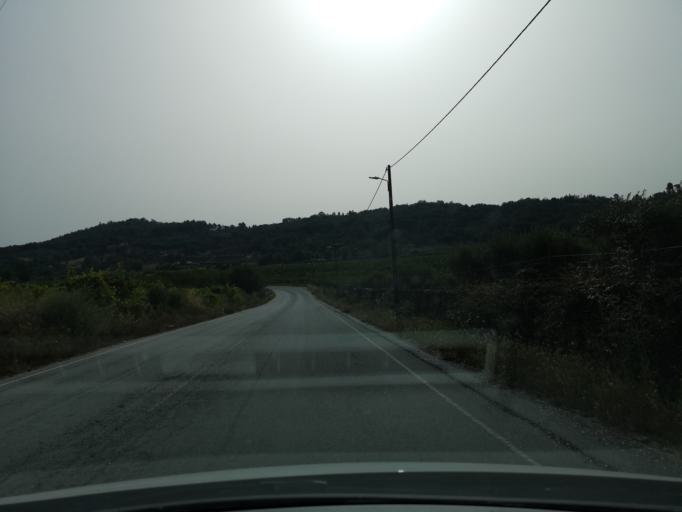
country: PT
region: Castelo Branco
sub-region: Belmonte
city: Belmonte
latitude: 40.3656
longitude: -7.3381
